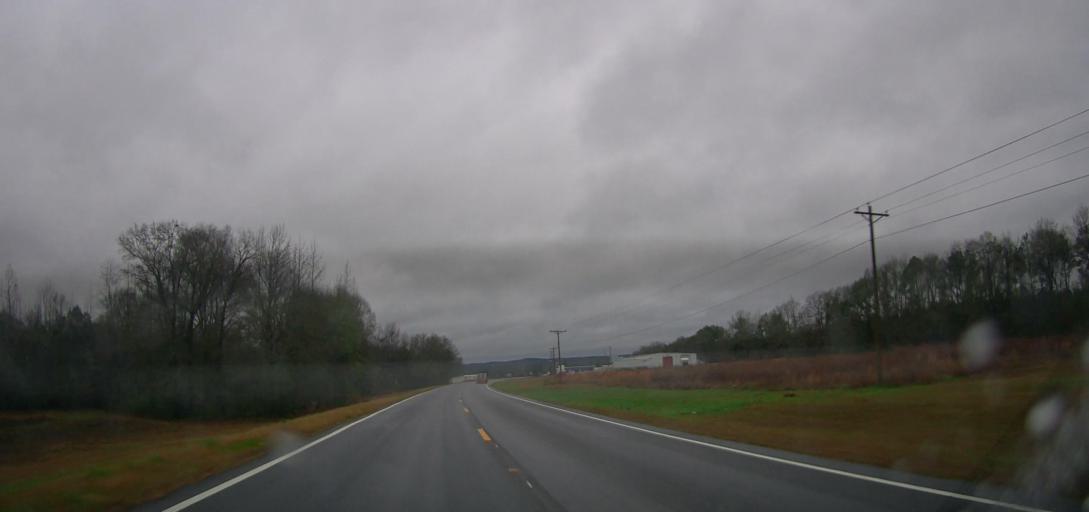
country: US
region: Alabama
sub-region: Chilton County
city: Thorsby
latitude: 32.7744
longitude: -86.8837
